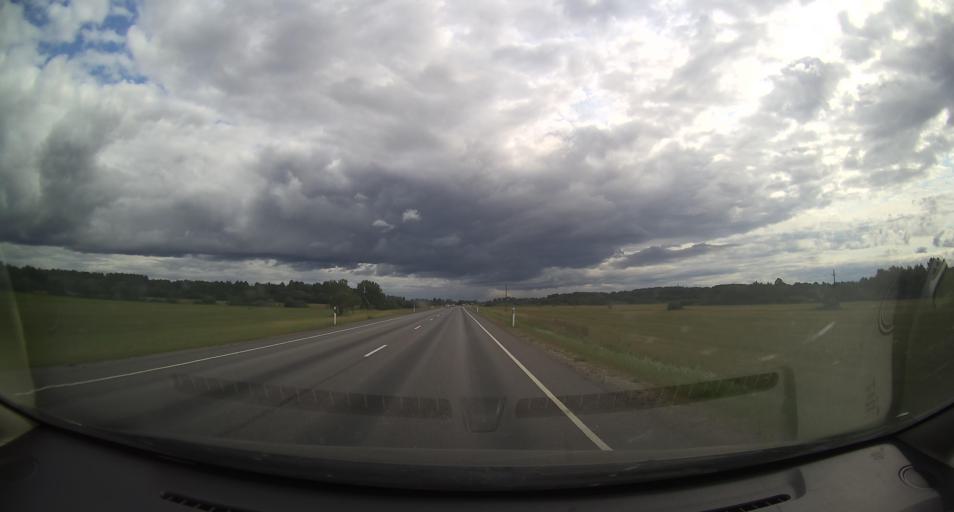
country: EE
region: Laeaene
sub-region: Lihula vald
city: Lihula
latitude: 58.7138
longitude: 23.8823
